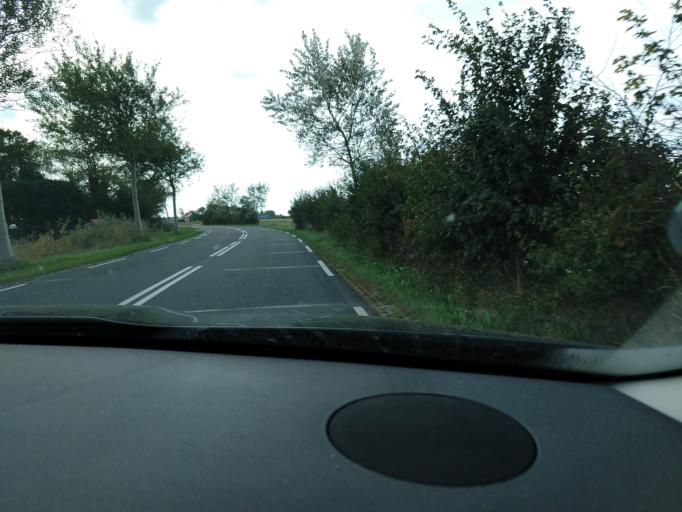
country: NL
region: Zeeland
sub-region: Gemeente Middelburg
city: Middelburg
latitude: 51.5216
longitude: 3.5313
